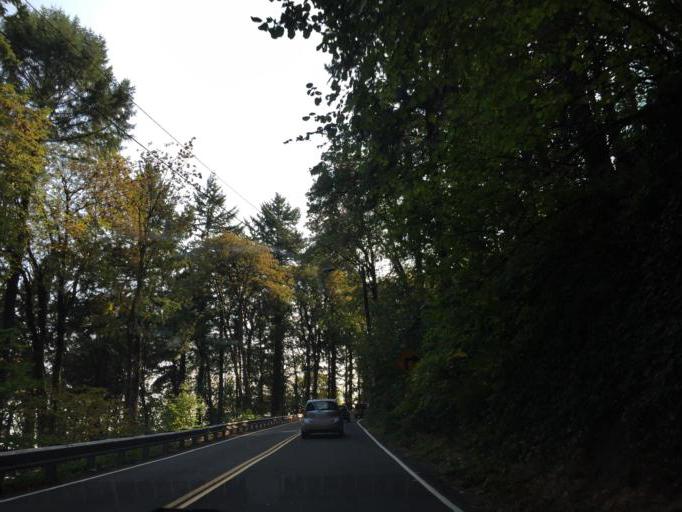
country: US
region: Oregon
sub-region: Multnomah County
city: Portland
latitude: 45.5019
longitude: -122.6857
